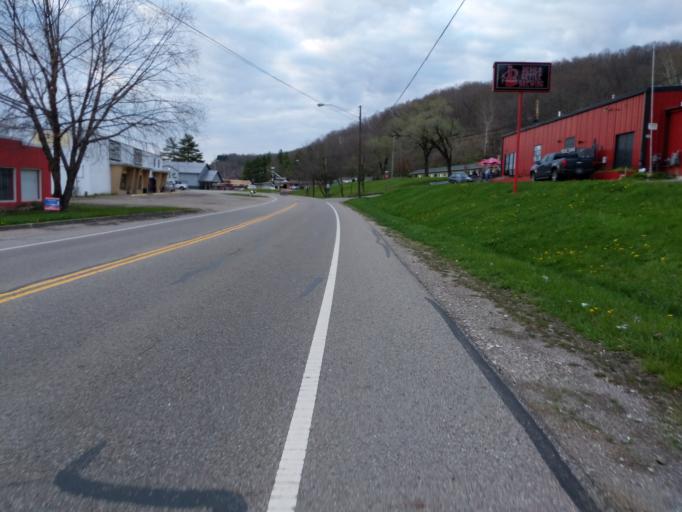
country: US
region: Ohio
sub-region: Athens County
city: Athens
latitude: 39.3487
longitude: -82.0956
